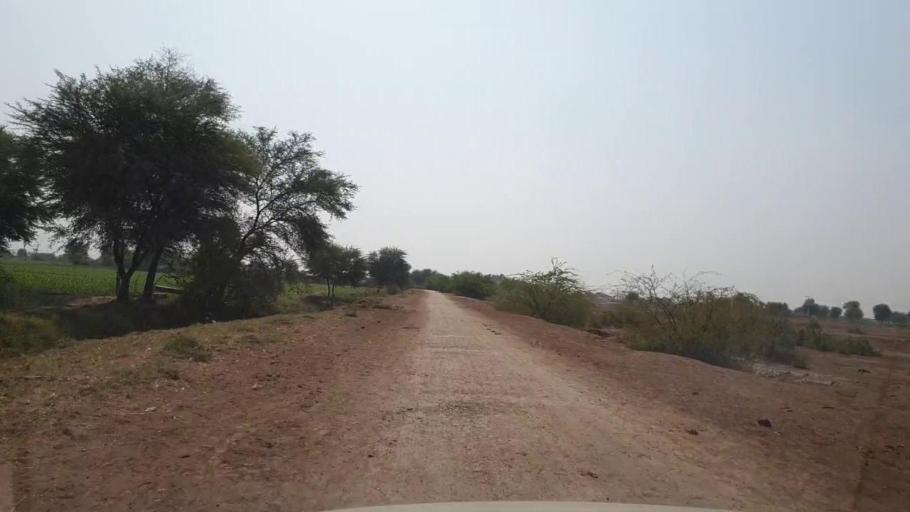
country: PK
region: Sindh
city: Dhoro Naro
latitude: 25.4799
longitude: 69.6406
